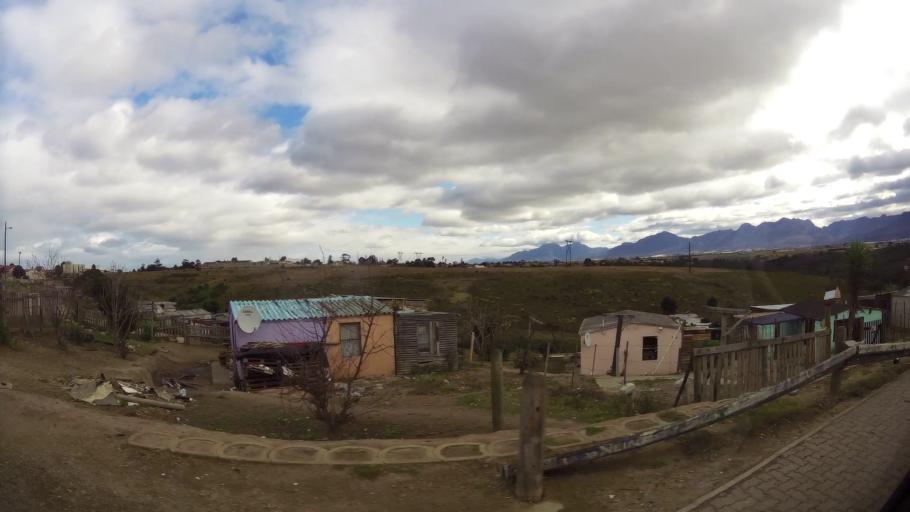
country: ZA
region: Western Cape
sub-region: Eden District Municipality
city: George
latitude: -34.0166
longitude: 22.4685
